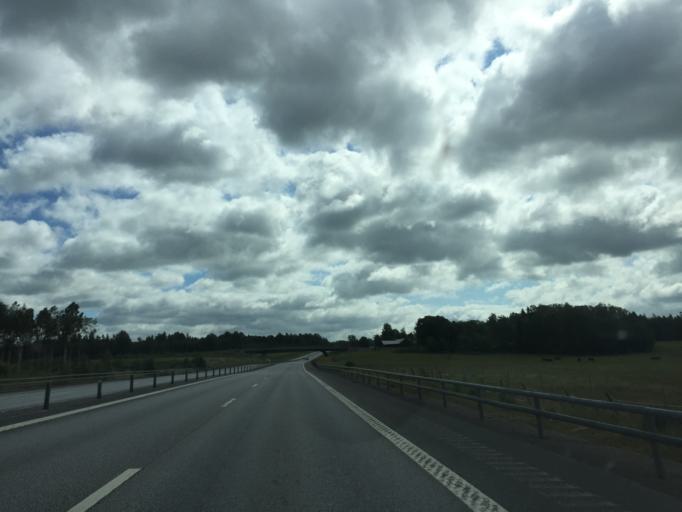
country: SE
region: OErebro
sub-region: Orebro Kommun
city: Vintrosa
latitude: 59.2540
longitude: 14.8964
